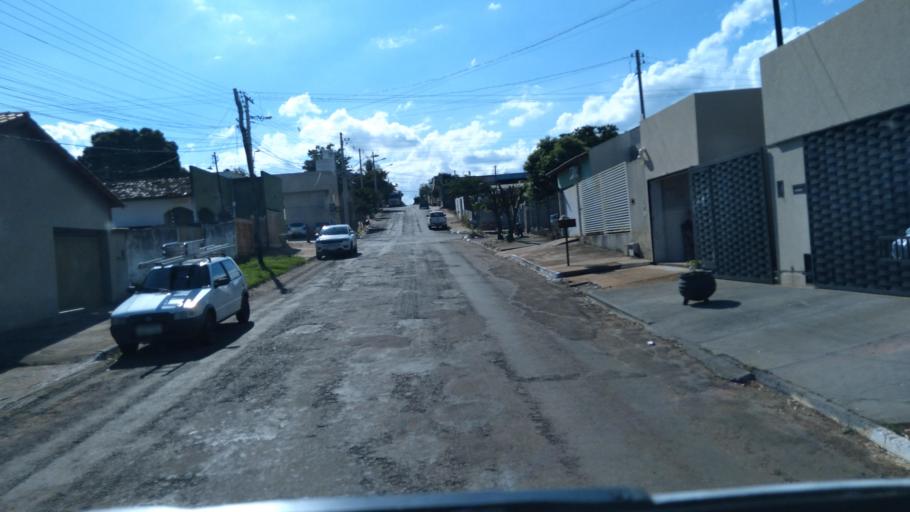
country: BR
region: Goias
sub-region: Mineiros
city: Mineiros
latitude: -17.5602
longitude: -52.5450
